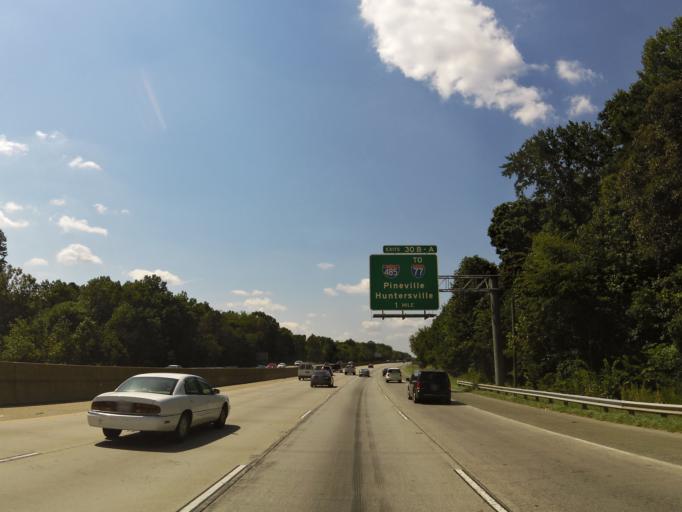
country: US
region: North Carolina
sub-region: Gaston County
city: Mount Holly
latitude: 35.2415
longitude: -80.9478
